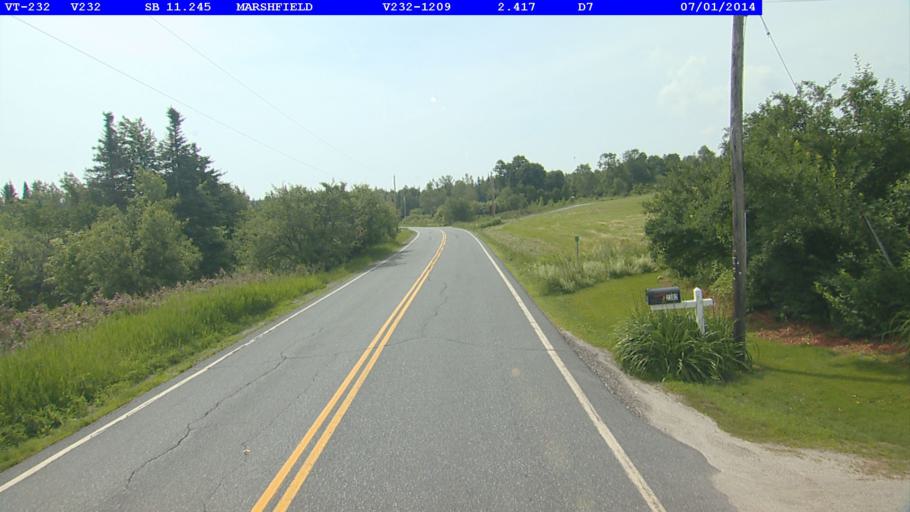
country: US
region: Vermont
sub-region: Caledonia County
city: Hardwick
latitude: 44.3420
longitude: -72.2952
